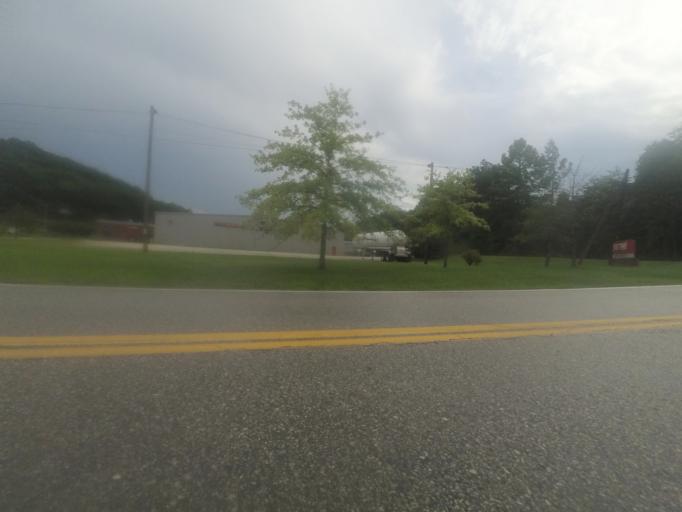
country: US
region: West Virginia
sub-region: Cabell County
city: Huntington
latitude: 38.3868
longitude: -82.3971
